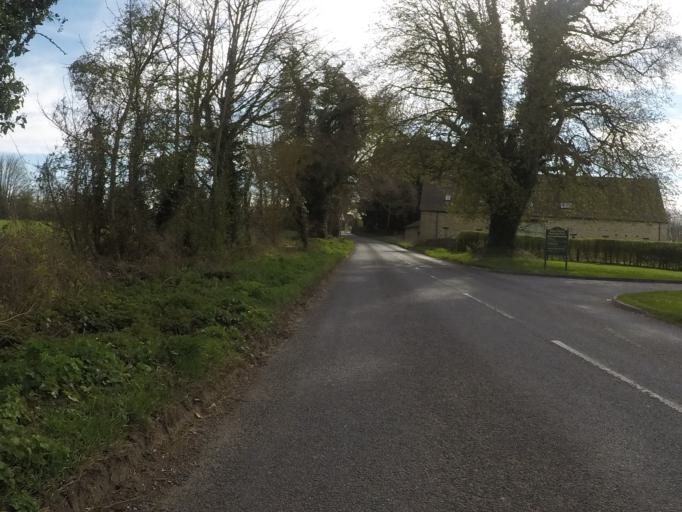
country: GB
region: England
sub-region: Oxfordshire
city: Charlbury
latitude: 51.8492
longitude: -1.4749
